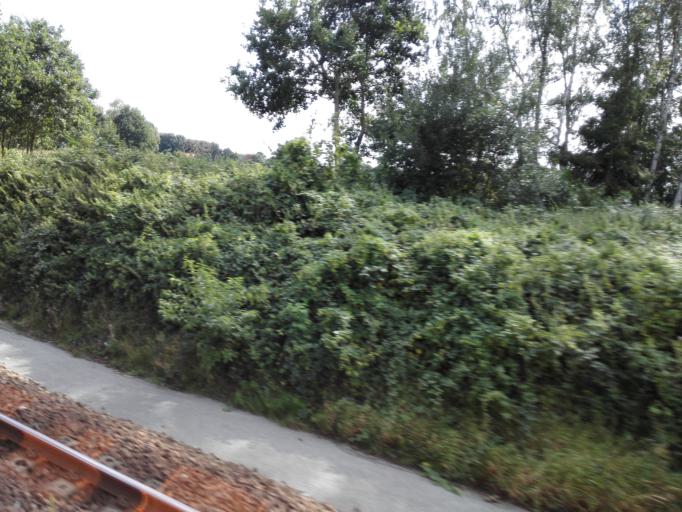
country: BE
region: Flanders
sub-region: Provincie Vlaams-Brabant
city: Boortmeerbeek
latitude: 50.9901
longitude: 4.5553
